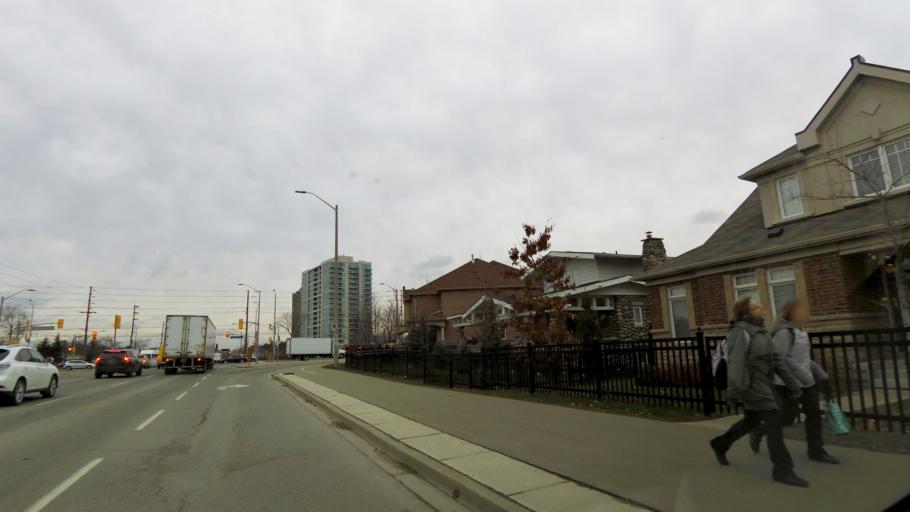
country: CA
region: Ontario
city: Mississauga
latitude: 43.5105
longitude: -79.6291
